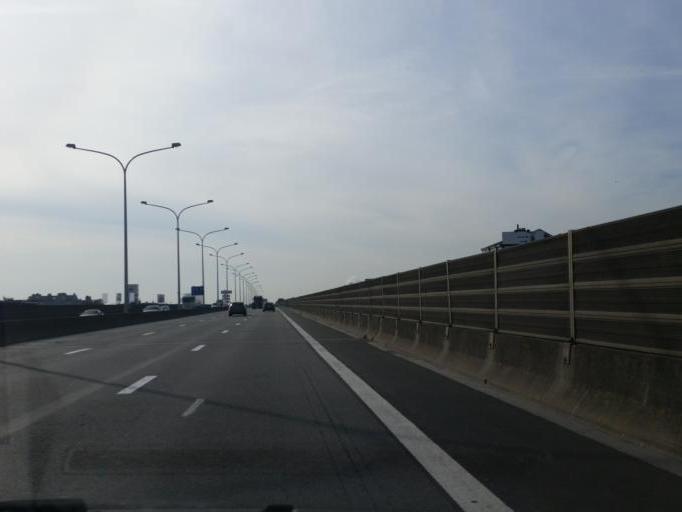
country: BE
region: Flanders
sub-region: Provincie Antwerpen
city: Aartselaar
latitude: 51.1669
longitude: 4.3859
